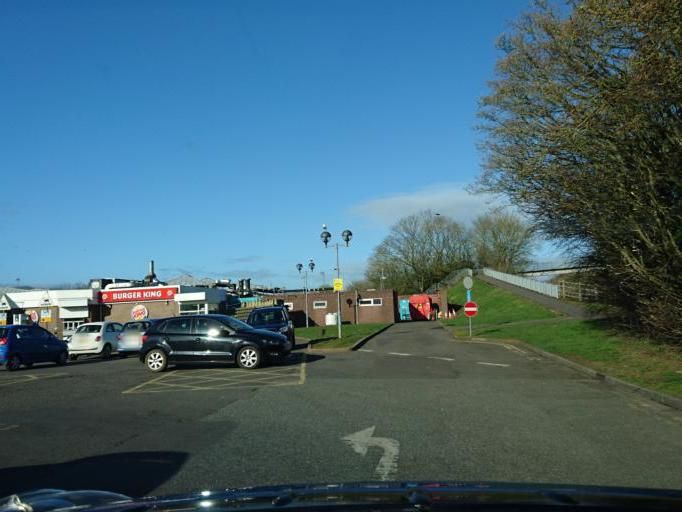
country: GB
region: England
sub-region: Wiltshire
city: Norton
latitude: 51.5102
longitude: -2.1578
